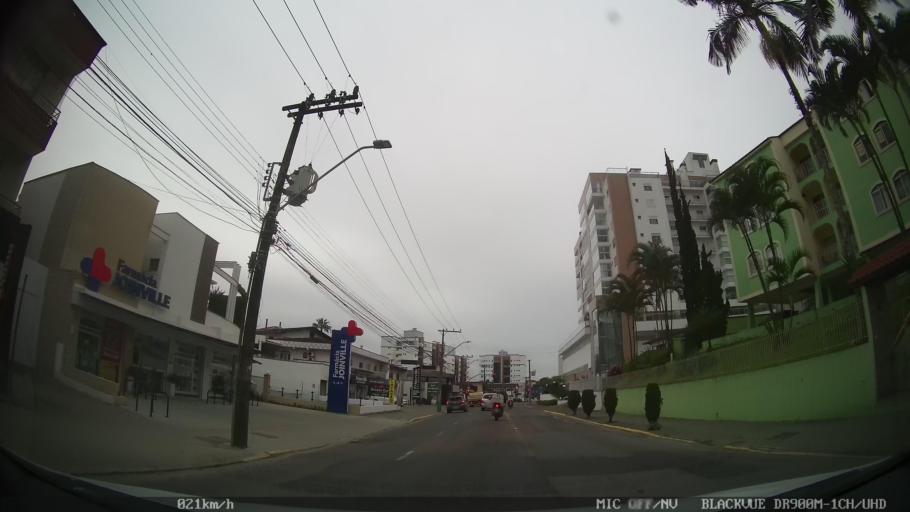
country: BR
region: Santa Catarina
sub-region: Joinville
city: Joinville
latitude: -26.2818
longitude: -48.8387
